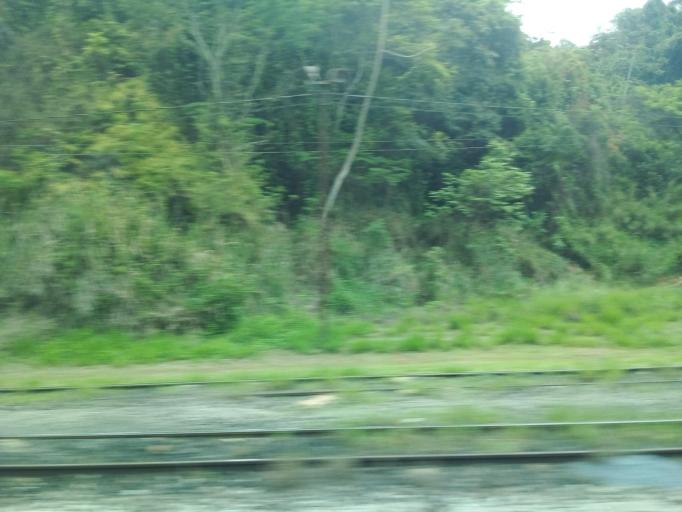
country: BR
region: Minas Gerais
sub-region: Joao Monlevade
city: Joao Monlevade
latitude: -19.8455
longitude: -43.1244
